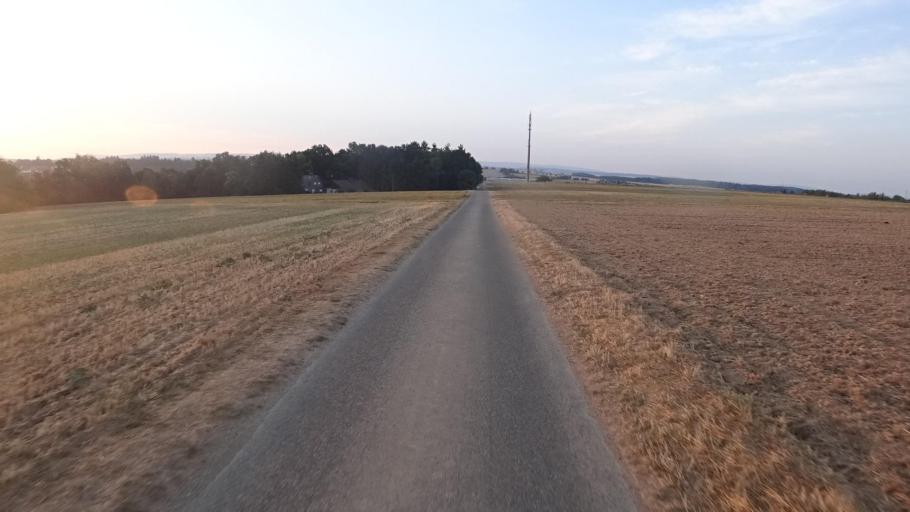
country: DE
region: Rheinland-Pfalz
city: Keidelheim
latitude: 49.9821
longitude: 7.5060
